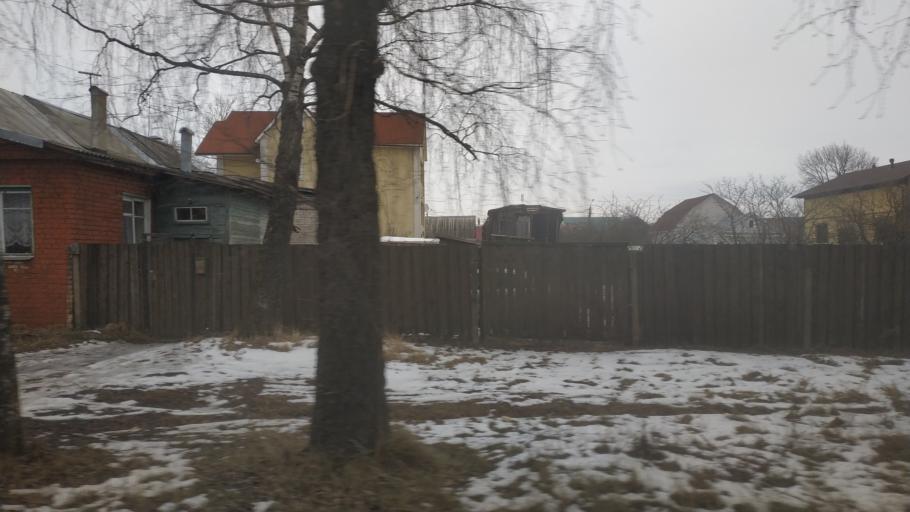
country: RU
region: Tverskaya
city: Tver
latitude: 56.8927
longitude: 35.8507
